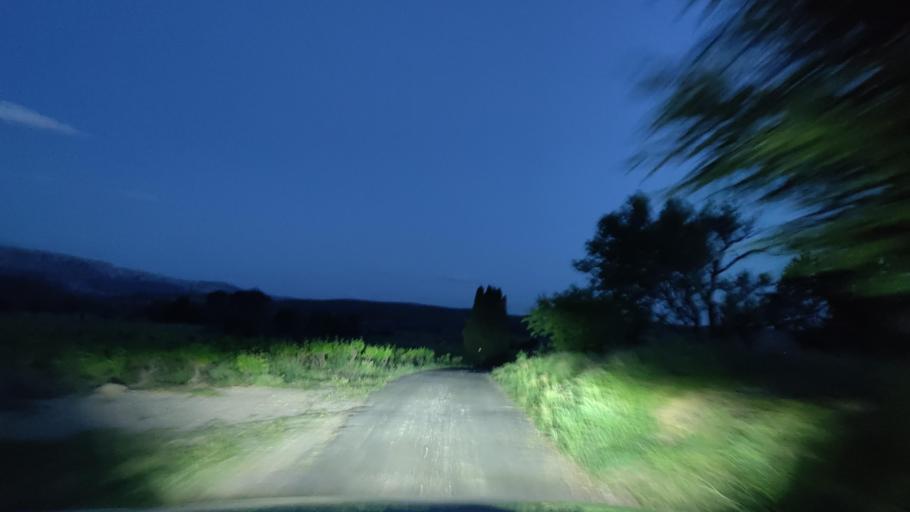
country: FR
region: Languedoc-Roussillon
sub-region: Departement des Pyrenees-Orientales
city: Estagel
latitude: 42.8759
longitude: 2.7297
